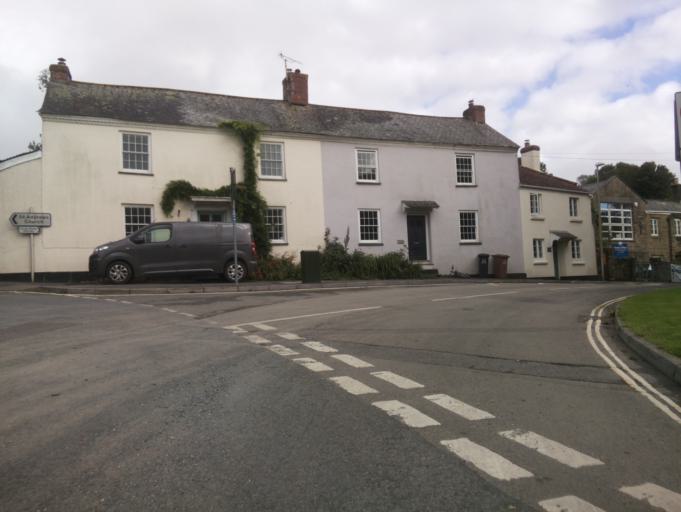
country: GB
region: England
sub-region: Devon
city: Modbury
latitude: 50.3151
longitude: -3.8360
